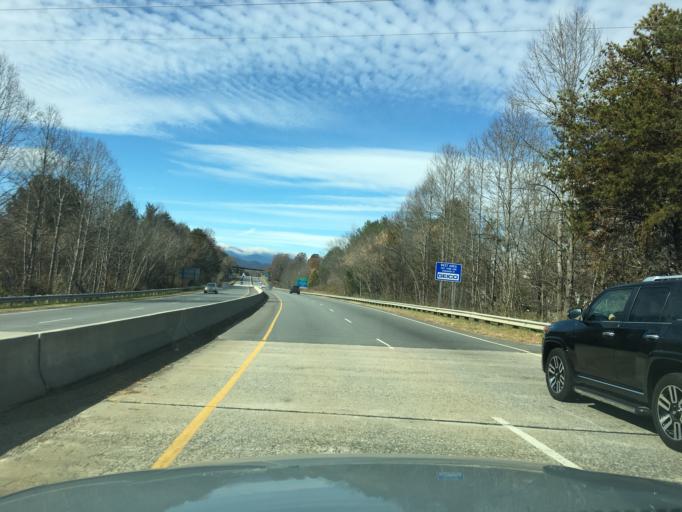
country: US
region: North Carolina
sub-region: McDowell County
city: Marion
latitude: 35.6734
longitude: -82.0151
